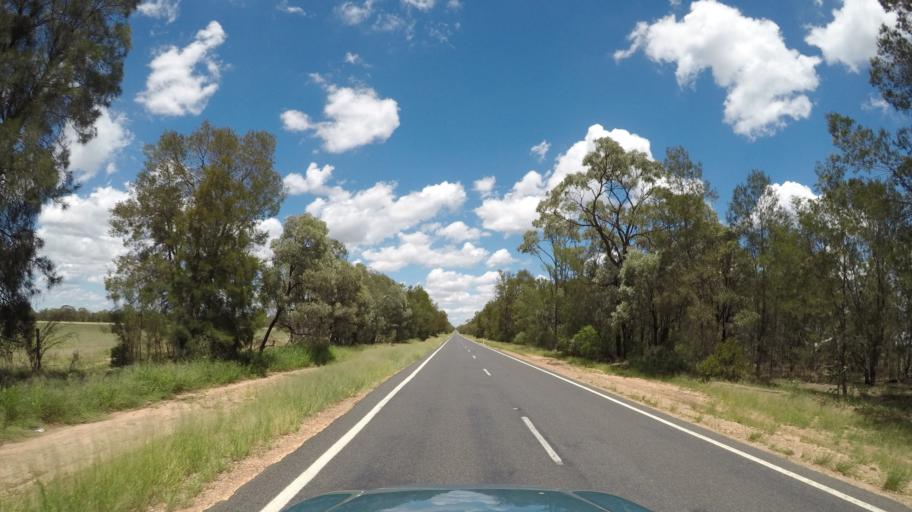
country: AU
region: Queensland
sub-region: Goondiwindi
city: Goondiwindi
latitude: -28.0065
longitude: 150.8861
